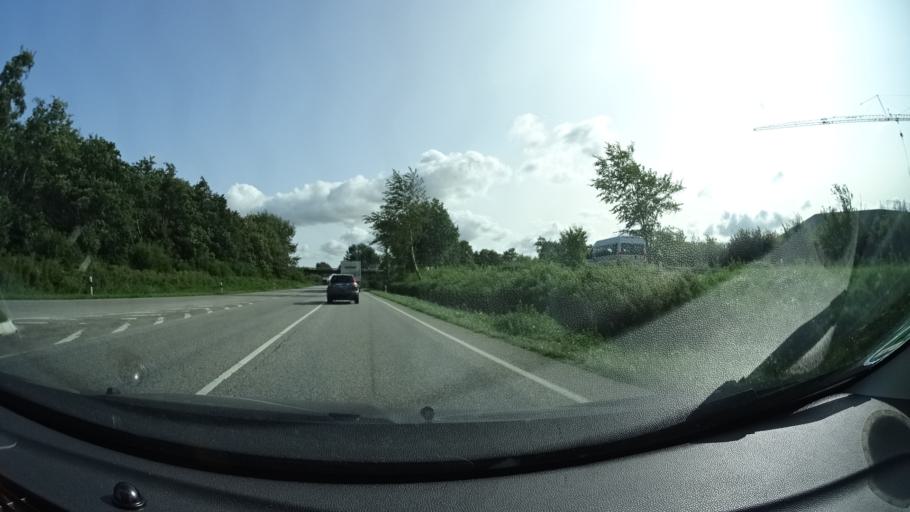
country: DE
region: Schleswig-Holstein
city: Tonning
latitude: 54.3266
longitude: 8.9541
